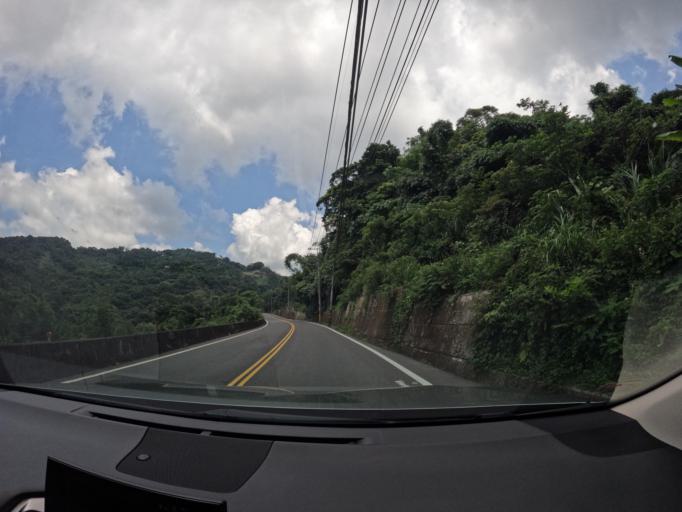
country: TW
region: Taiwan
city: Fengyuan
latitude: 24.3834
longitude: 120.8027
